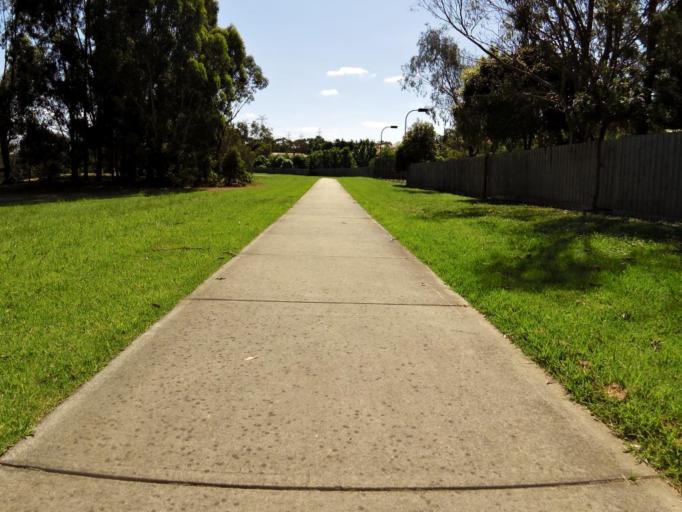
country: AU
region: Victoria
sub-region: Casey
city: Endeavour Hills
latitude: -37.9568
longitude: 145.2705
